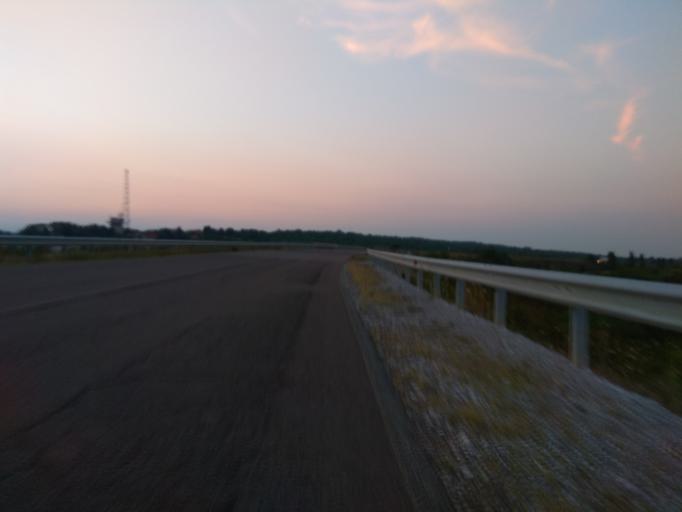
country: HU
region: Borsod-Abauj-Zemplen
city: Emod
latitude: 47.9350
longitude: 20.8278
